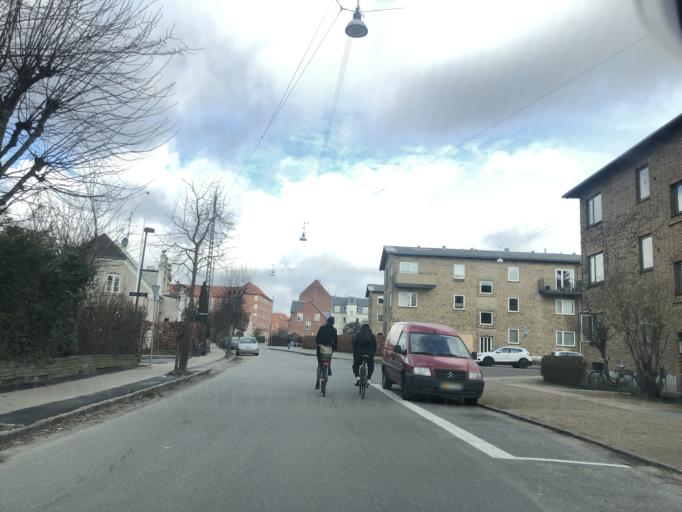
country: DK
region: Capital Region
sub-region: Tarnby Kommune
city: Tarnby
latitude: 55.6496
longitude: 12.6175
